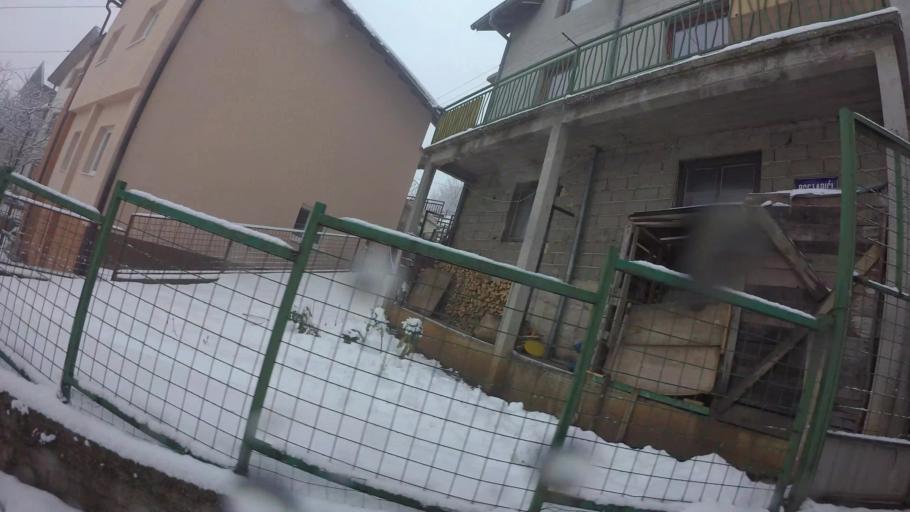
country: BA
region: Federation of Bosnia and Herzegovina
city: Kobilja Glava
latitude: 43.8454
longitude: 18.4295
